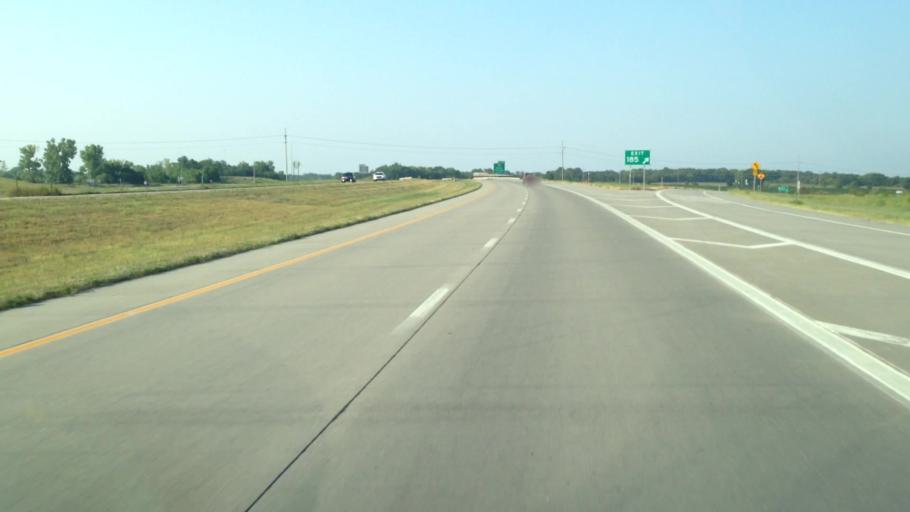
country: US
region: Kansas
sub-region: Franklin County
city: Ottawa
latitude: 38.5912
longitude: -95.2351
